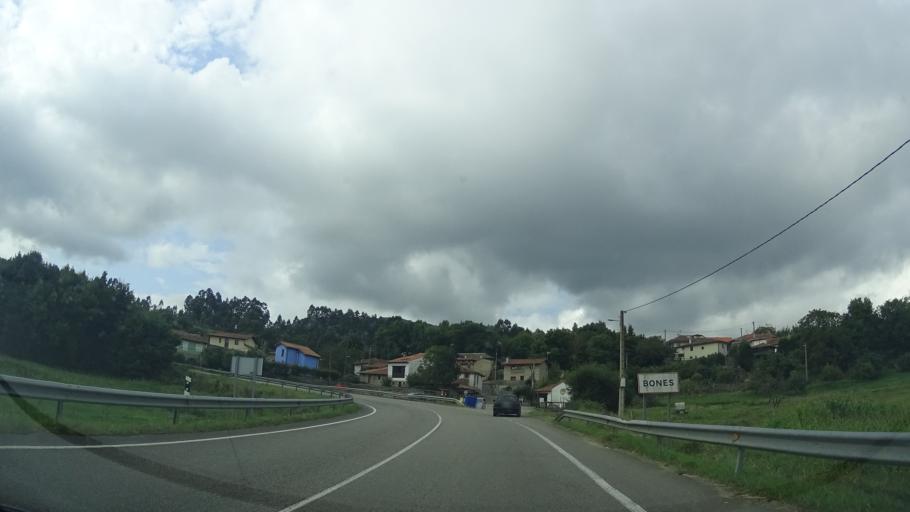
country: ES
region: Asturias
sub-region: Province of Asturias
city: Ribadesella
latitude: 43.4628
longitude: -5.1214
